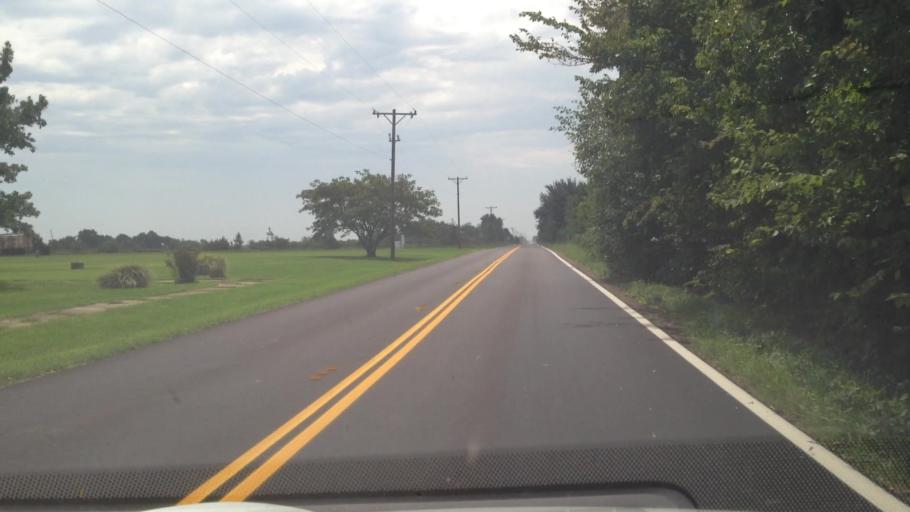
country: US
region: Kansas
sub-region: Crawford County
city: Girard
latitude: 37.6577
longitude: -94.9698
